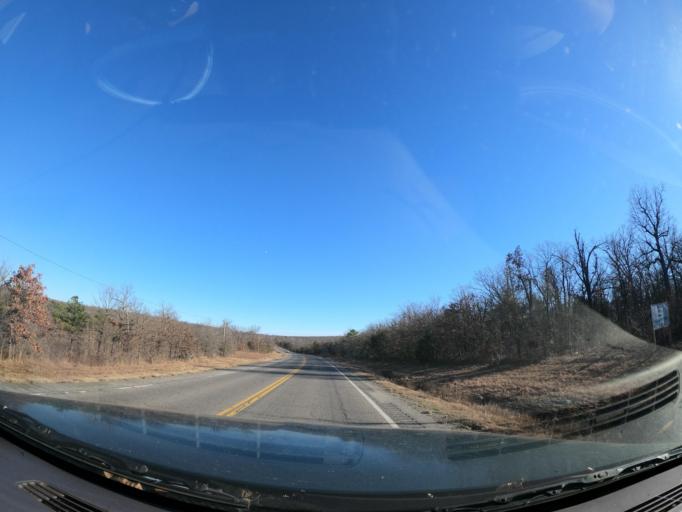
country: US
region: Oklahoma
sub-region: Pittsburg County
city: Longtown
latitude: 35.2269
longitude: -95.4486
